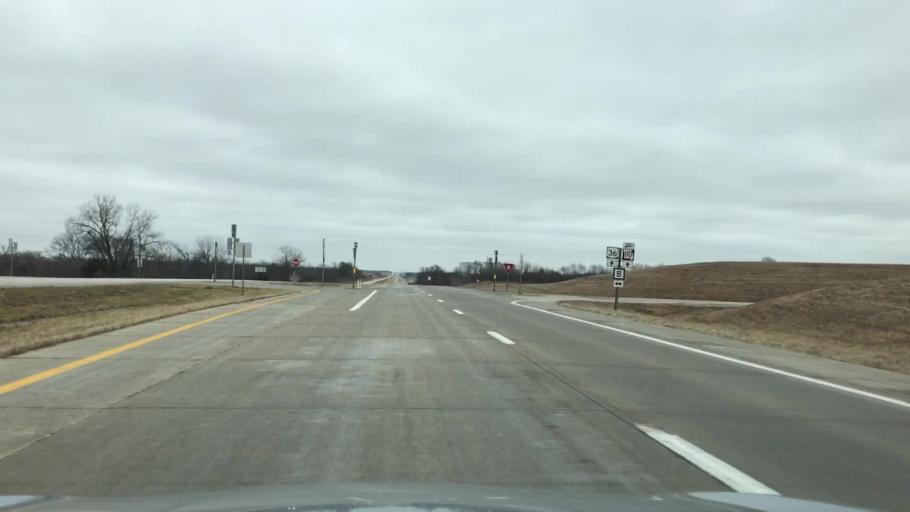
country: US
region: Missouri
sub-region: Caldwell County
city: Hamilton
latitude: 39.7354
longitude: -93.9273
